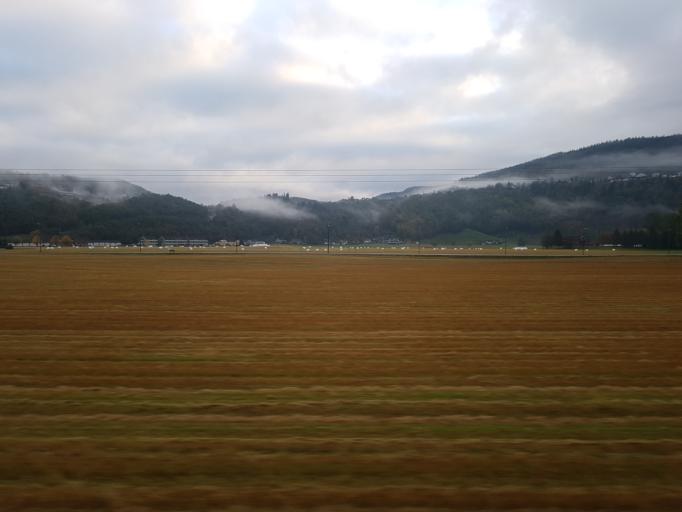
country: NO
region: Sor-Trondelag
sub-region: Melhus
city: Melhus
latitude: 63.2814
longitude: 10.2891
